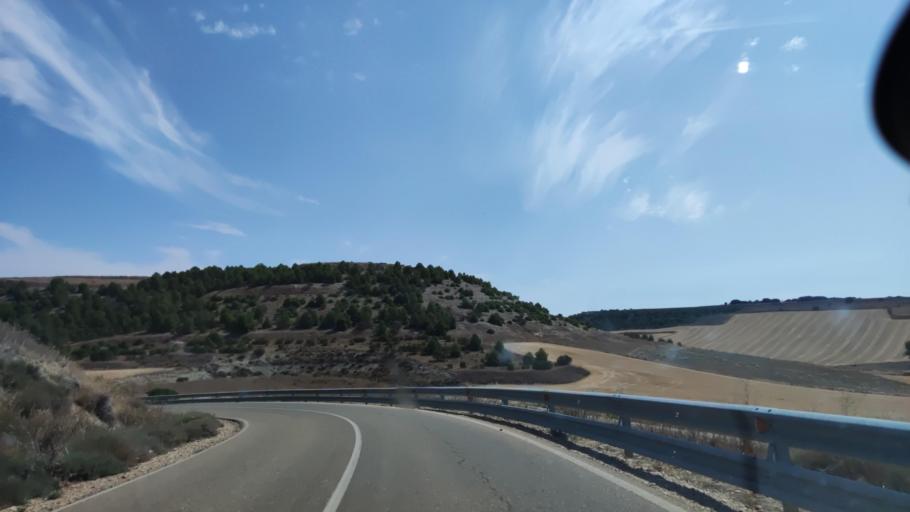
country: ES
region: Castille and Leon
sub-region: Provincia de Valladolid
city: Uruena
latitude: 41.7229
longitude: -5.1948
